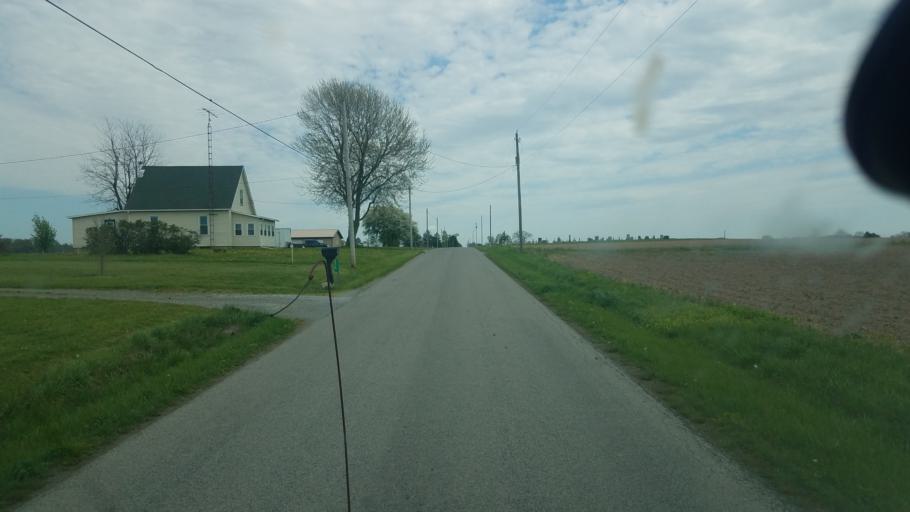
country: US
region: Ohio
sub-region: Allen County
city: Bluffton
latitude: 40.8118
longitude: -83.9457
